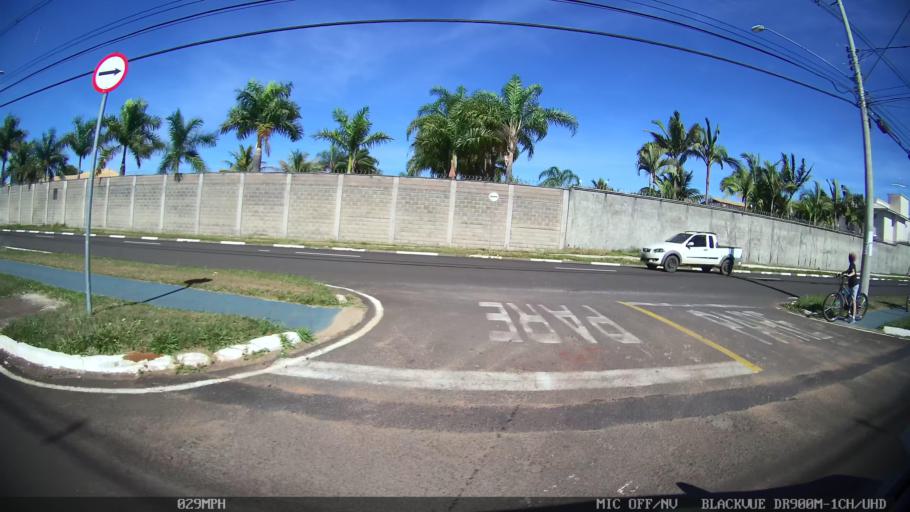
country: BR
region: Sao Paulo
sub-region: Franca
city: Franca
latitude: -20.5622
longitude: -47.3689
